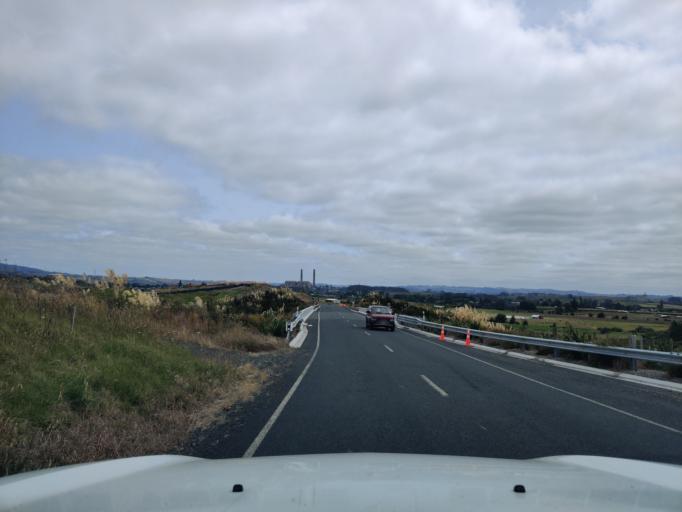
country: NZ
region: Waikato
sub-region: Waikato District
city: Te Kauwhata
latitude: -37.5228
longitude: 175.1757
